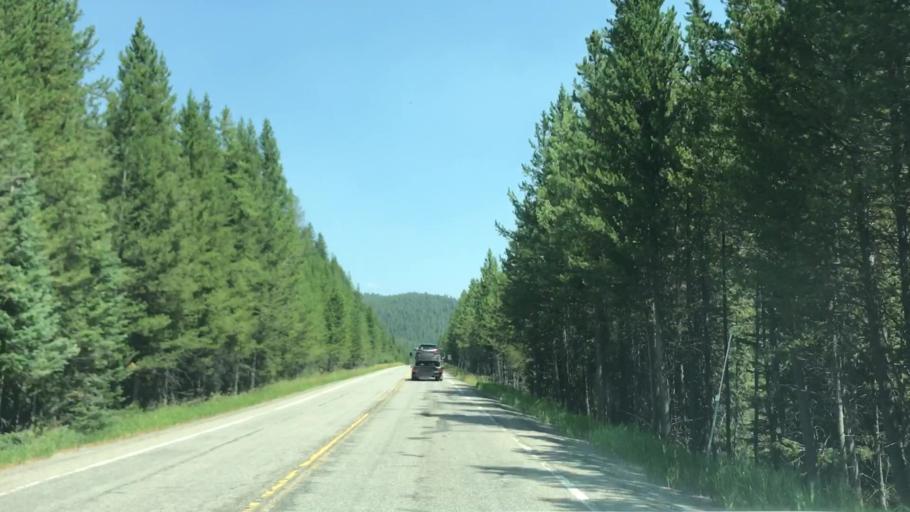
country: US
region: Montana
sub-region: Gallatin County
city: West Yellowstone
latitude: 44.8120
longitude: -111.0940
